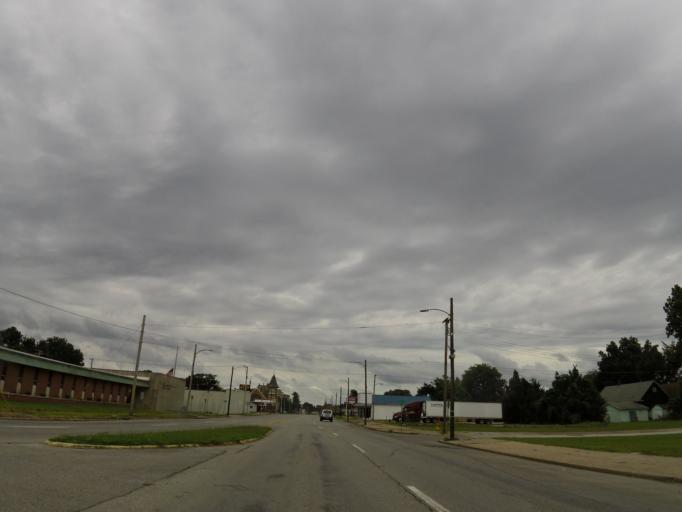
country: US
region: Illinois
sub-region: Alexander County
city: Cairo
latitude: 37.0055
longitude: -89.1771
